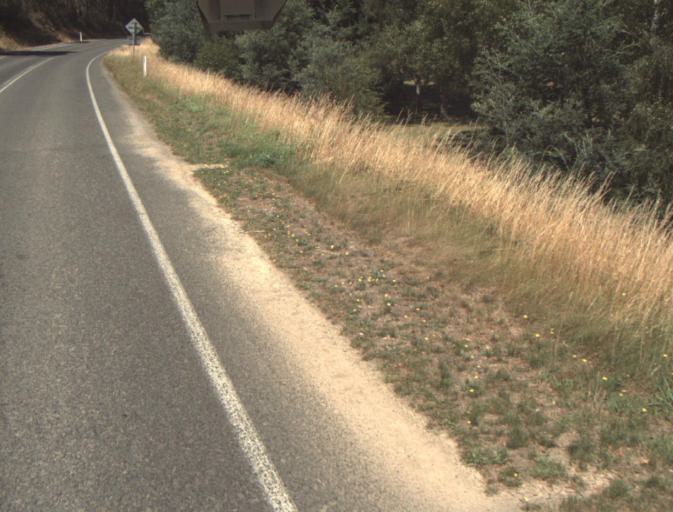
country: AU
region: Tasmania
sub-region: Dorset
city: Scottsdale
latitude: -41.3113
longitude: 147.3678
